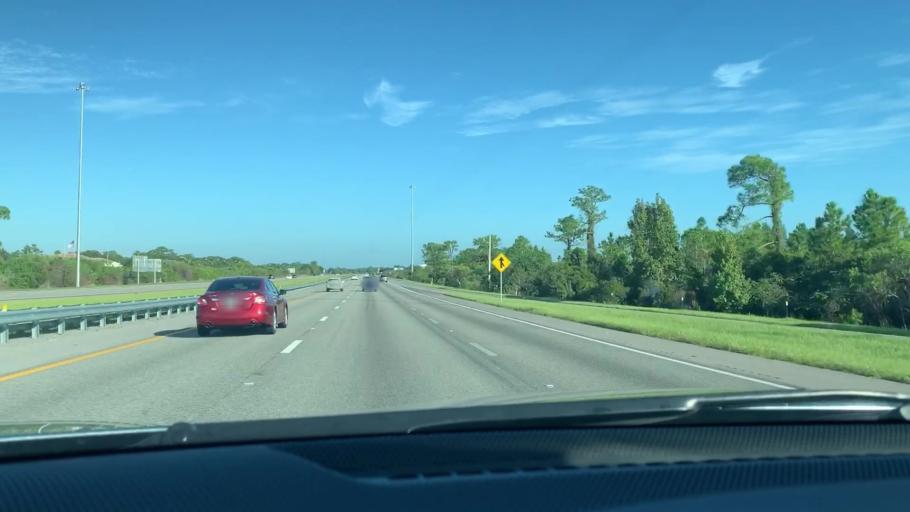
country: US
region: Florida
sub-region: Charlotte County
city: Harbour Heights
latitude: 27.0235
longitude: -82.0499
